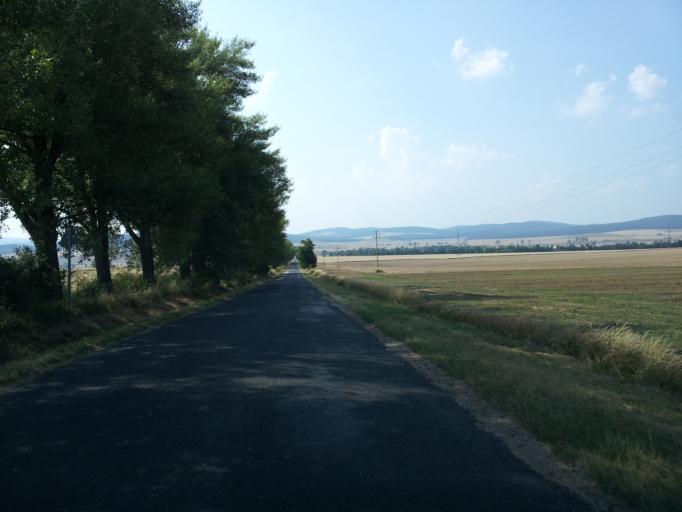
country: HU
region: Veszprem
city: Nemesvamos
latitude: 47.0170
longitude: 17.8090
